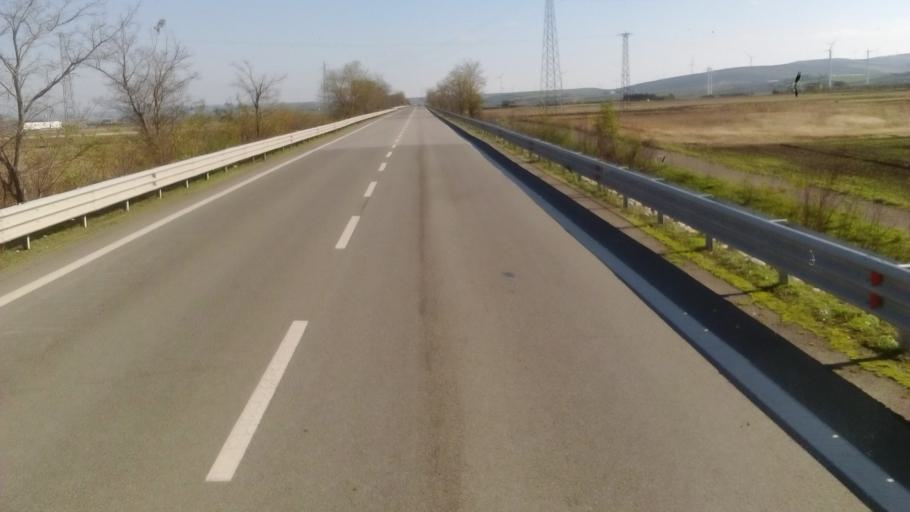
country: IT
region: Basilicate
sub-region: Provincia di Potenza
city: Zona 179
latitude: 41.0783
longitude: 15.6346
